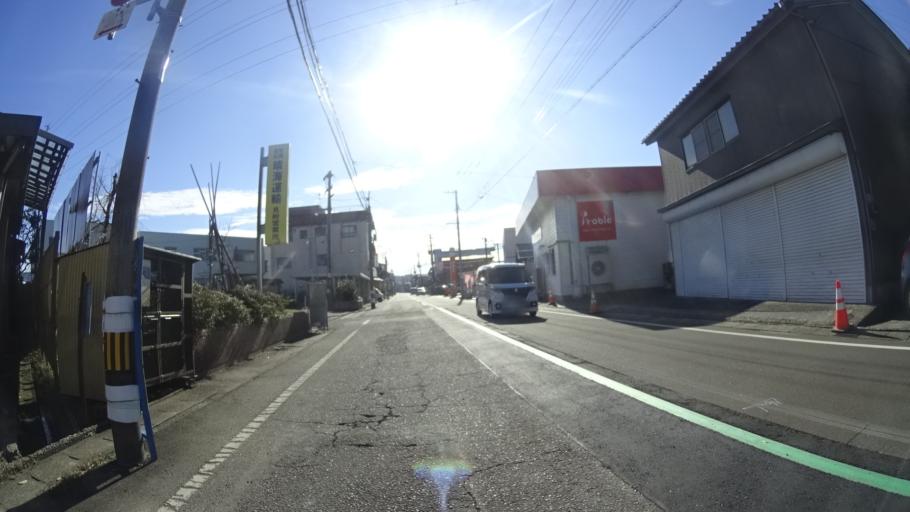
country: JP
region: Niigata
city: Mitsuke
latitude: 37.5323
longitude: 138.9196
